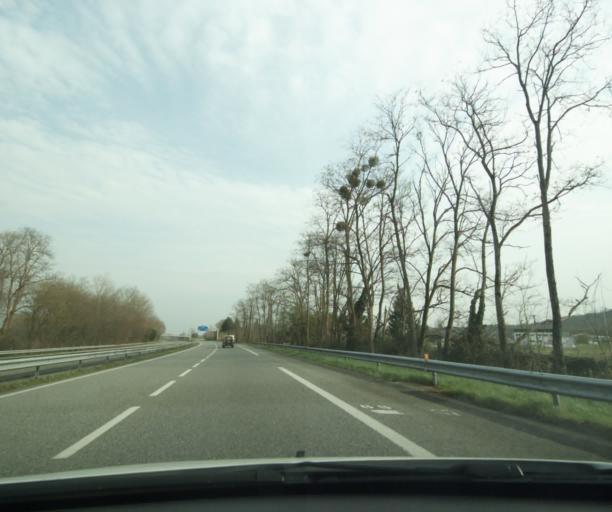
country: FR
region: Aquitaine
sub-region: Departement des Pyrenees-Atlantiques
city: Orthez
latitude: 43.4707
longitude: -0.7535
